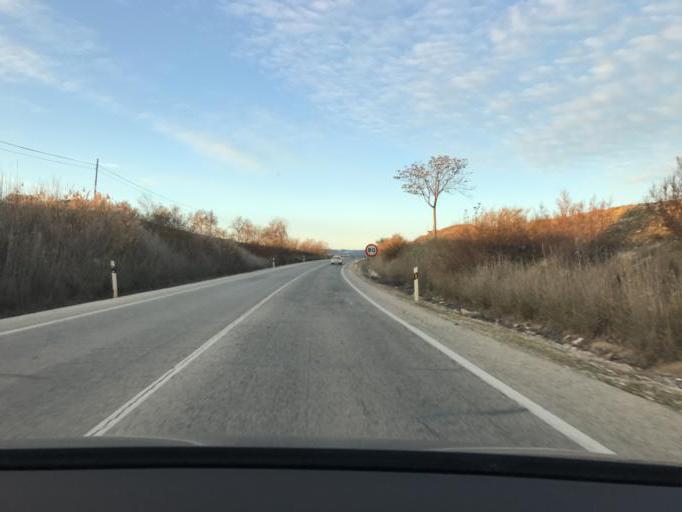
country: ES
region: Andalusia
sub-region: Provincia de Jaen
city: Jodar
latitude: 37.9207
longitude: -3.3517
